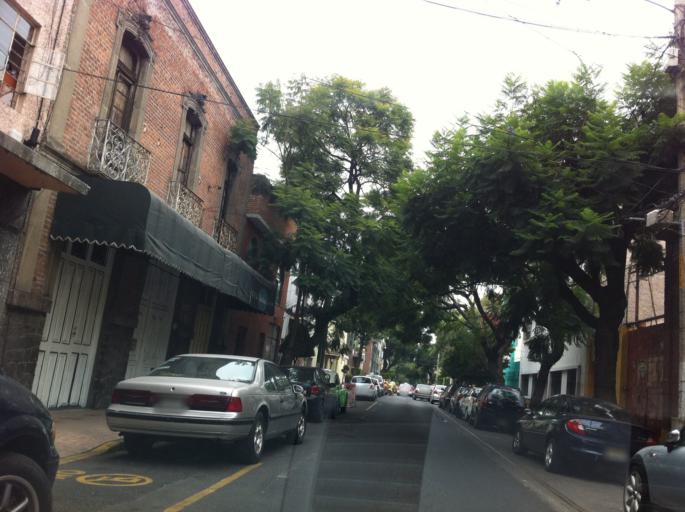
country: MX
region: Mexico City
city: Azcapotzalco
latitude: 19.4580
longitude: -99.1790
